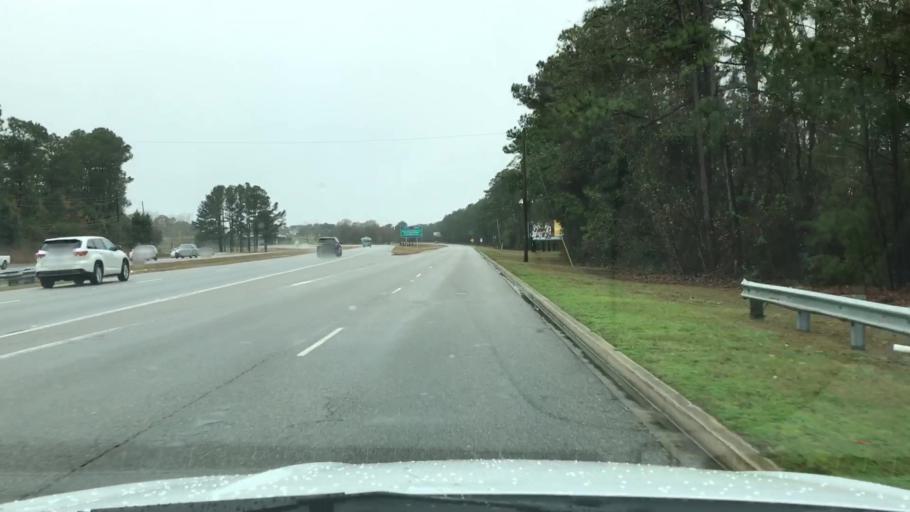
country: US
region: South Carolina
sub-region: Horry County
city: Myrtle Beach
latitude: 33.7721
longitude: -78.8011
